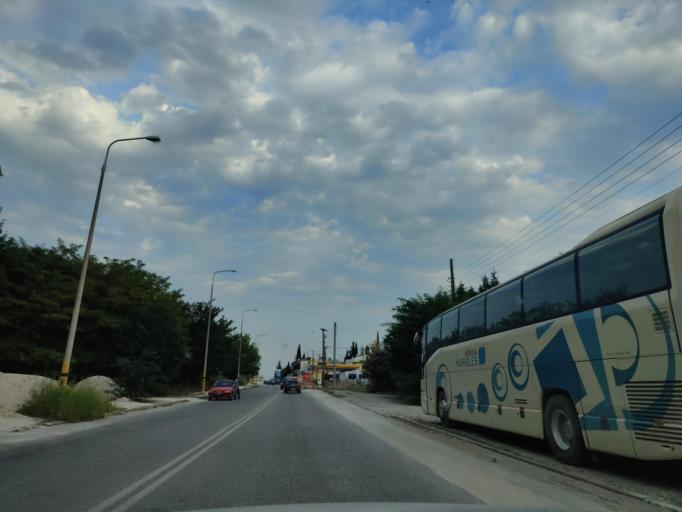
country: GR
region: East Macedonia and Thrace
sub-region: Nomos Dramas
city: Drama
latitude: 41.1520
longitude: 24.1330
